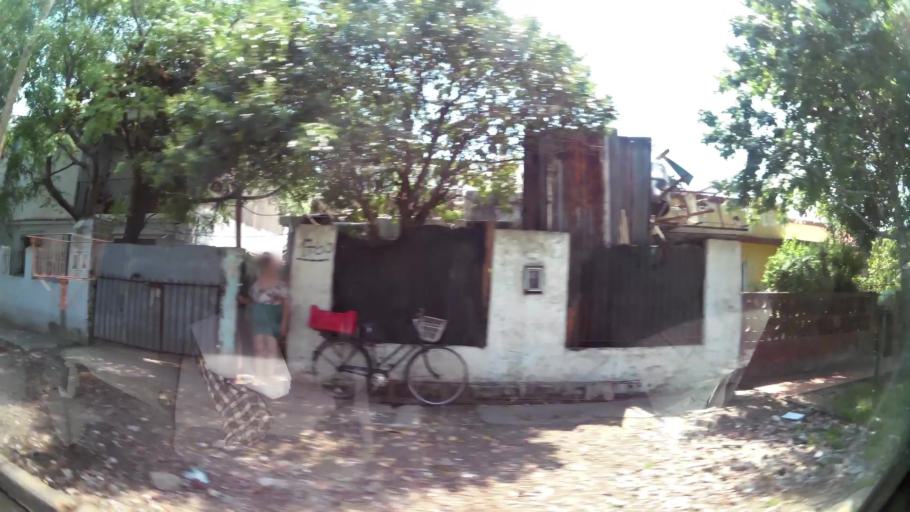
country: AR
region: Buenos Aires
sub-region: Partido de Tigre
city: Tigre
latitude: -34.4382
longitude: -58.5820
